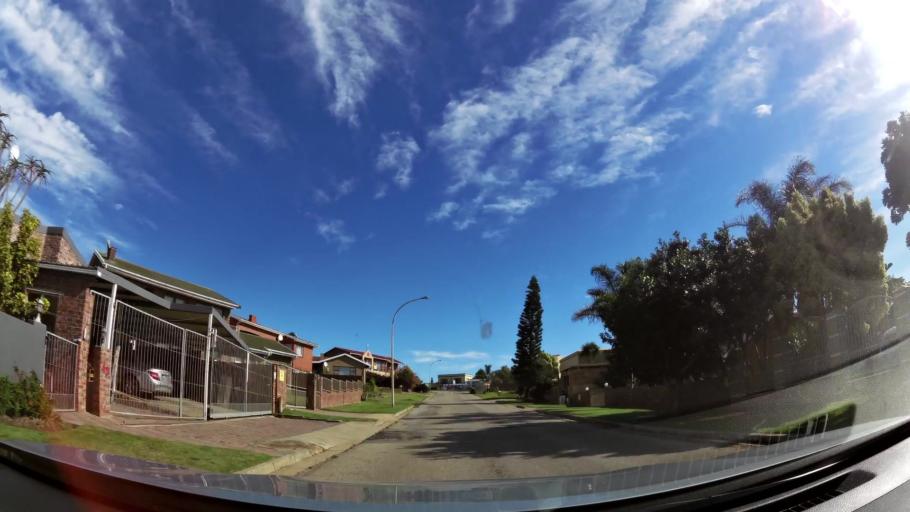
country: ZA
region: Eastern Cape
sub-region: Cacadu District Municipality
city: Jeffrey's Bay
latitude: -34.0150
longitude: 24.9242
